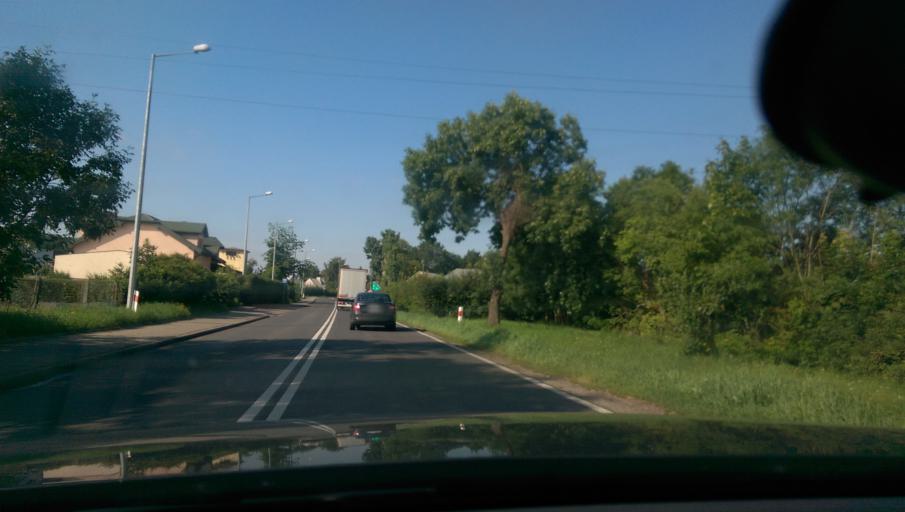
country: PL
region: Masovian Voivodeship
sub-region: Powiat plonski
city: Plonsk
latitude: 52.6340
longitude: 20.3889
